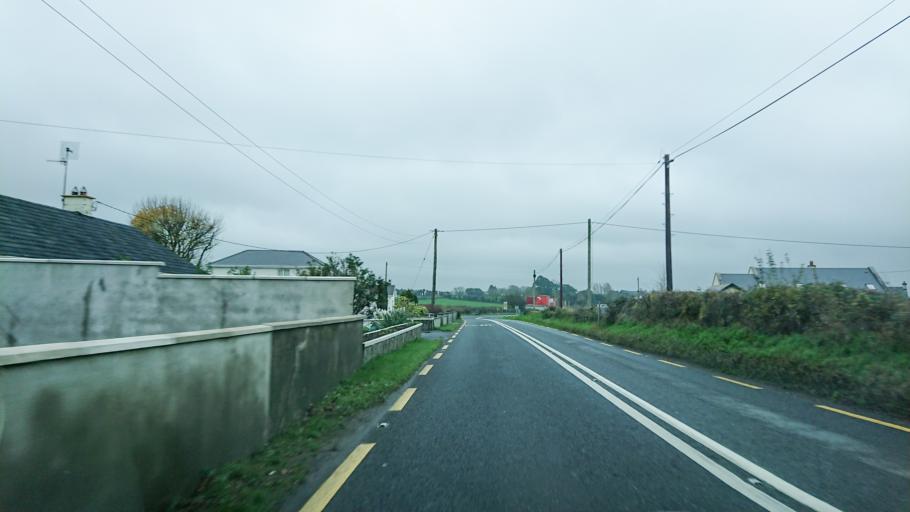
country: IE
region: Leinster
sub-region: Kilkenny
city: Mooncoin
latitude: 52.3014
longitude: -7.2719
